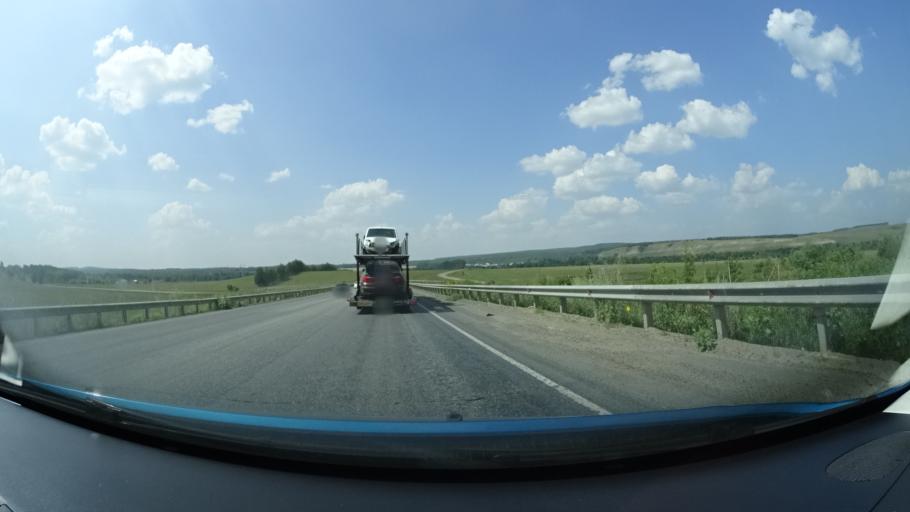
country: RU
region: Bashkortostan
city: Nizhnetroitskiy
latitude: 54.4560
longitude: 53.6794
